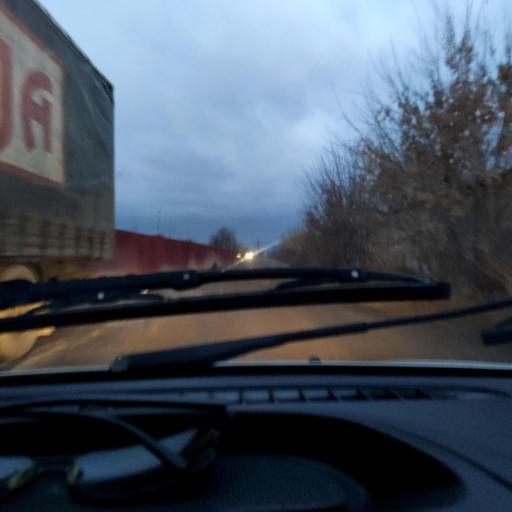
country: RU
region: Samara
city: Tol'yatti
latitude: 53.5661
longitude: 49.4835
